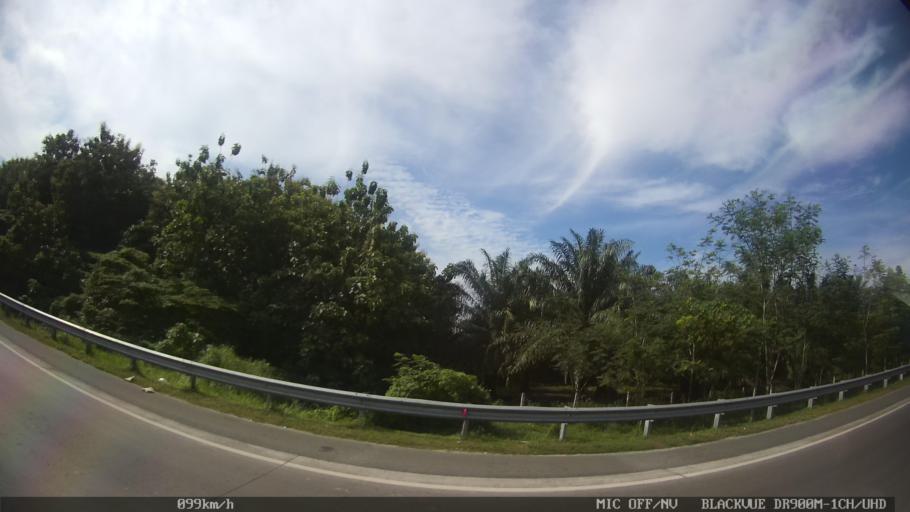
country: ID
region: North Sumatra
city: Sunggal
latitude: 3.6384
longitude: 98.6111
